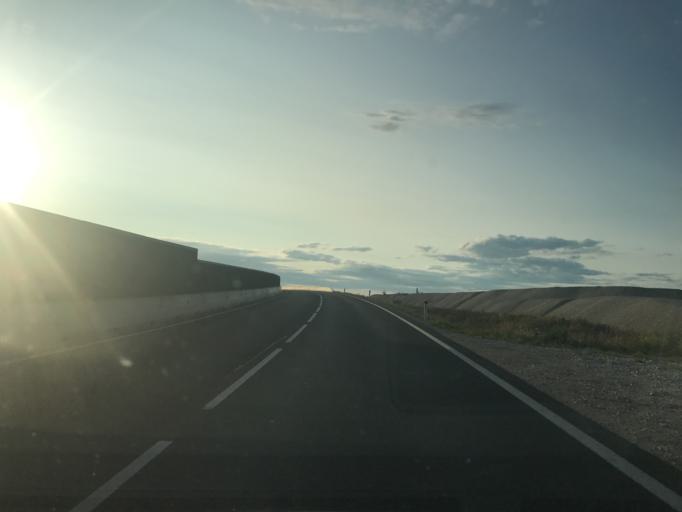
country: AT
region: Lower Austria
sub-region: Politischer Bezirk Wiener Neustadt
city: Lichtenworth
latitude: 47.8437
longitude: 16.2782
